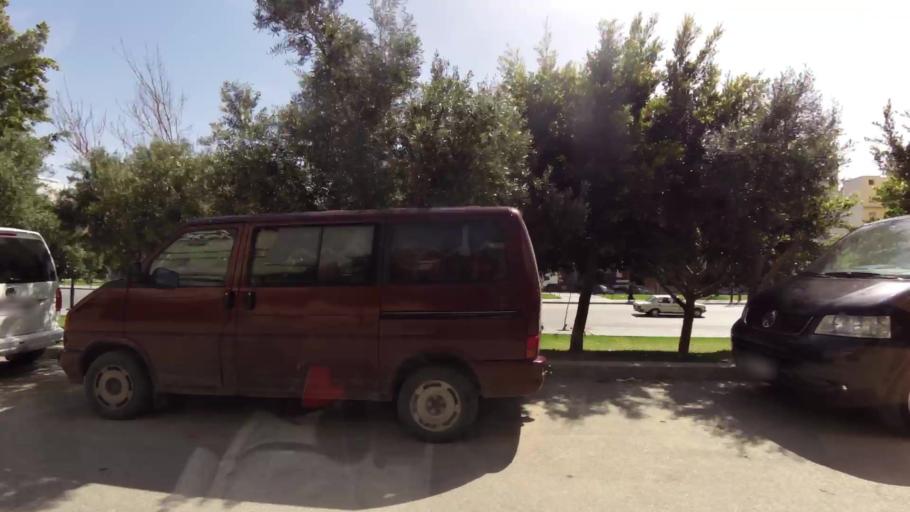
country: MA
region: Tanger-Tetouan
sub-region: Tanger-Assilah
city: Tangier
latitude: 35.7396
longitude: -5.8011
